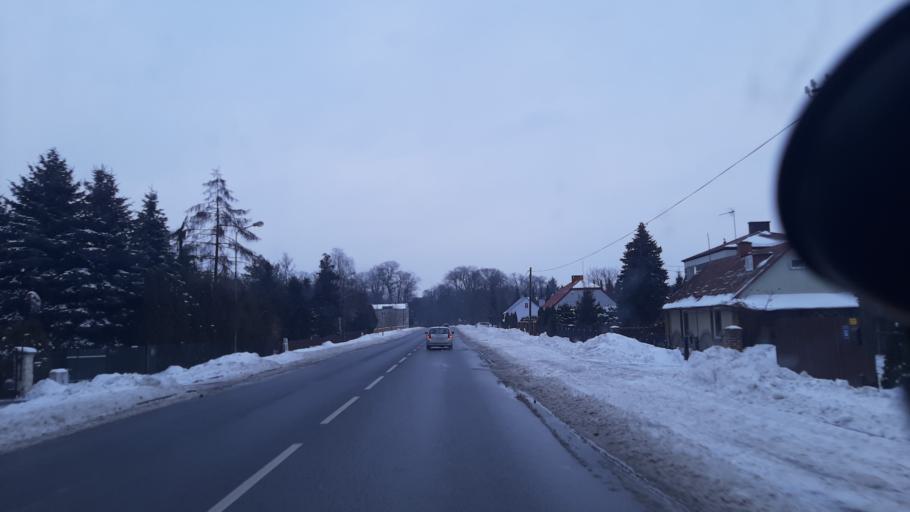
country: PL
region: Lublin Voivodeship
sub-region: Powiat lubelski
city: Garbow
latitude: 51.3562
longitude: 22.3256
